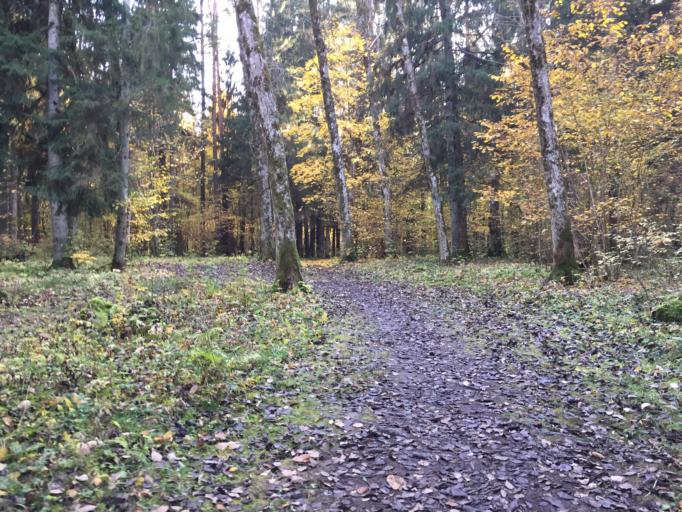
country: LV
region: Saldus Rajons
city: Saldus
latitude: 56.6486
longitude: 22.4876
